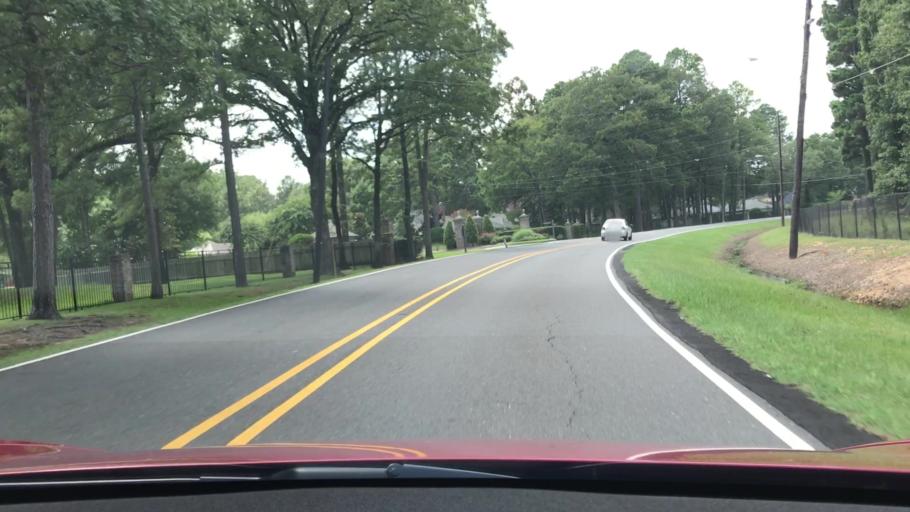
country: US
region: Louisiana
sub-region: De Soto Parish
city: Stonewall
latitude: 32.3663
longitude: -93.6990
